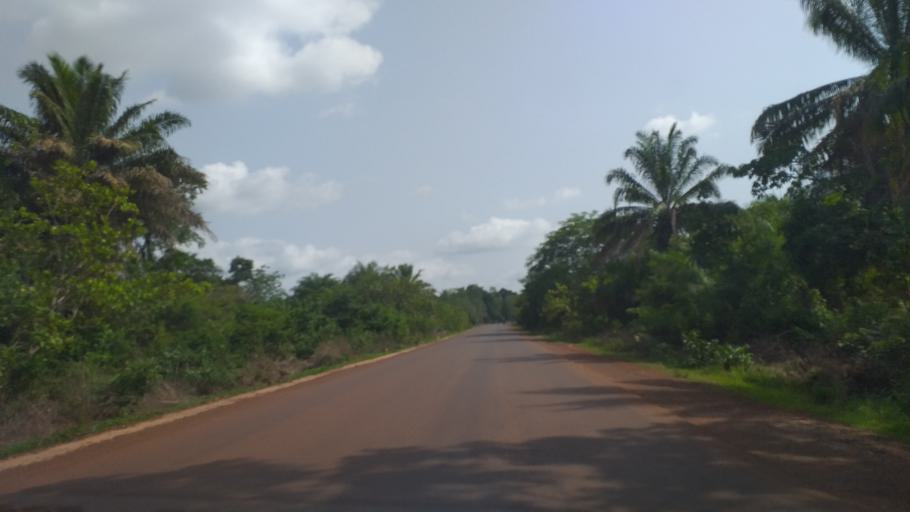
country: GN
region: Boke
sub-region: Boke Prefecture
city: Sangueya
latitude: 10.8241
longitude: -14.3719
